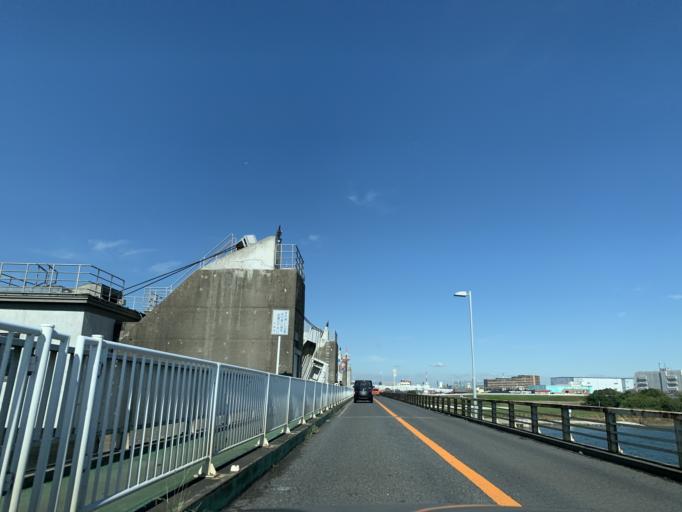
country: JP
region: Tokyo
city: Urayasu
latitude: 35.7025
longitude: 139.9229
